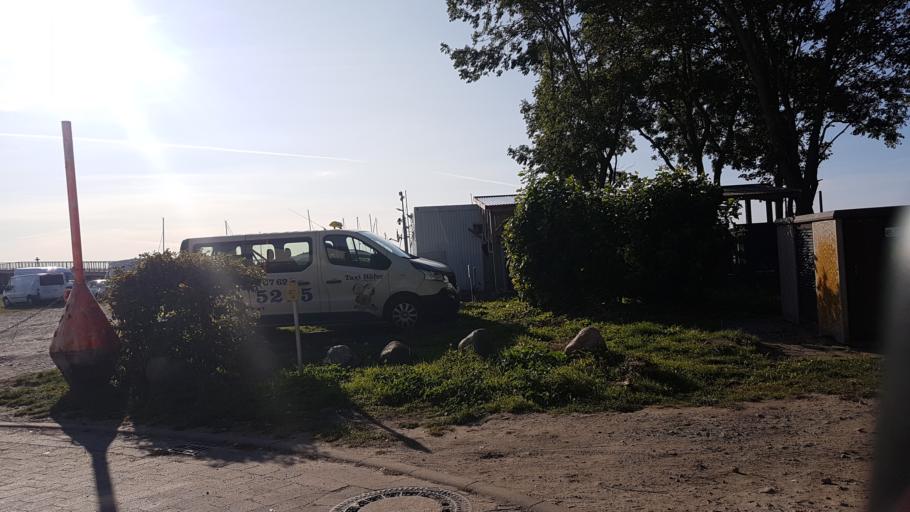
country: DE
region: Mecklenburg-Vorpommern
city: Wiek
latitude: 54.6228
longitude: 13.2867
